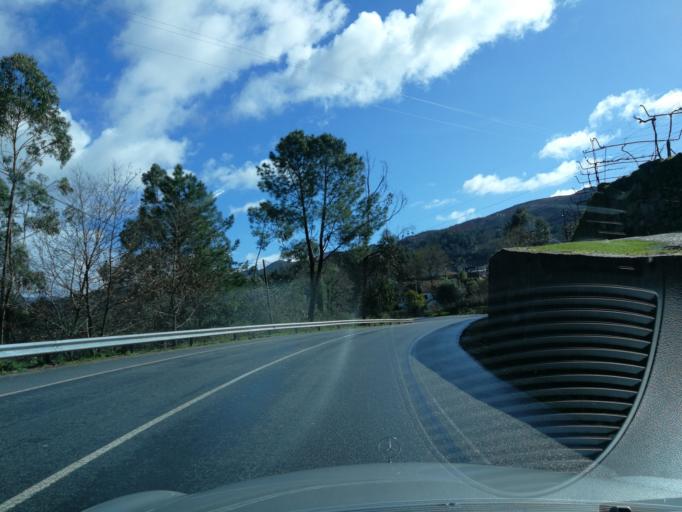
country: PT
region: Braga
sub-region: Terras de Bouro
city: Antas
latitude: 41.8351
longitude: -8.2985
